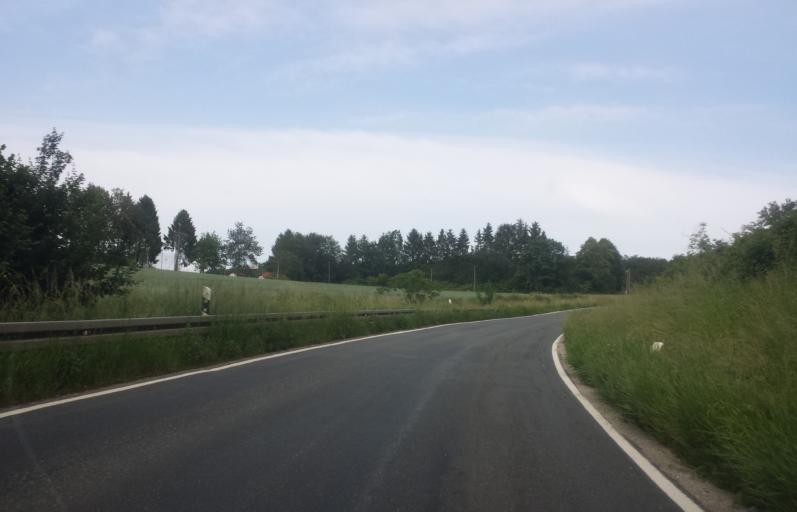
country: DE
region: Bavaria
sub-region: Regierungsbezirk Mittelfranken
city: Wachenroth
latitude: 49.7881
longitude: 10.7029
